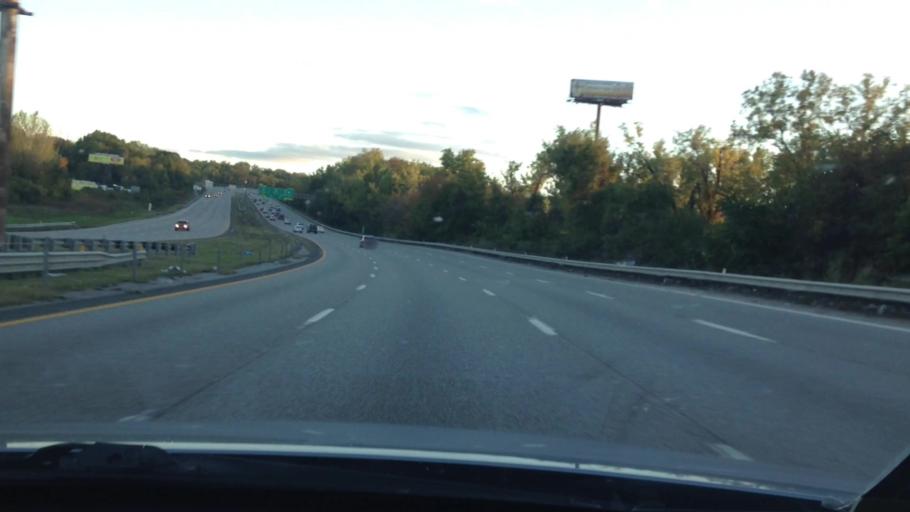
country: US
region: Missouri
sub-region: Jackson County
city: Sugar Creek
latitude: 39.0798
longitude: -94.4911
